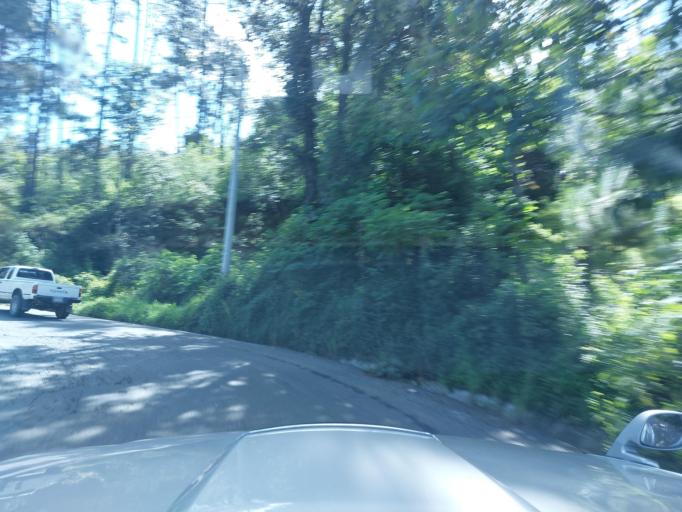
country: GT
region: Chimaltenango
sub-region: Municipio de San Juan Comalapa
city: Comalapa
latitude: 14.7111
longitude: -90.8916
